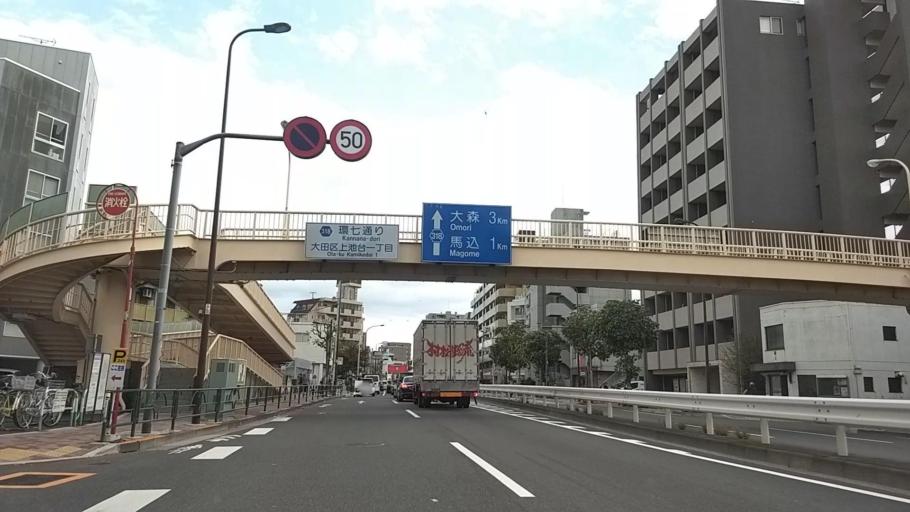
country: JP
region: Kanagawa
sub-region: Kawasaki-shi
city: Kawasaki
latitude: 35.6022
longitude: 139.6991
